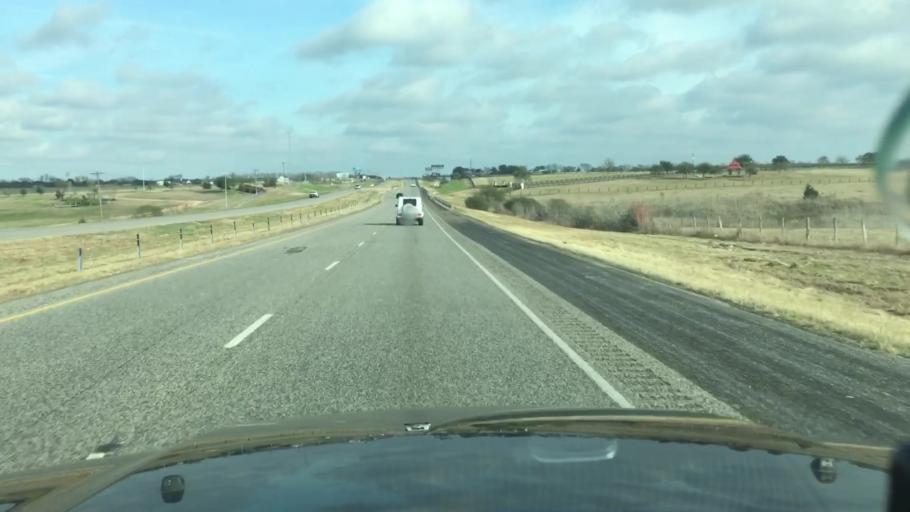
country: US
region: Texas
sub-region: Washington County
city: Brenham
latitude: 30.1387
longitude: -96.3094
